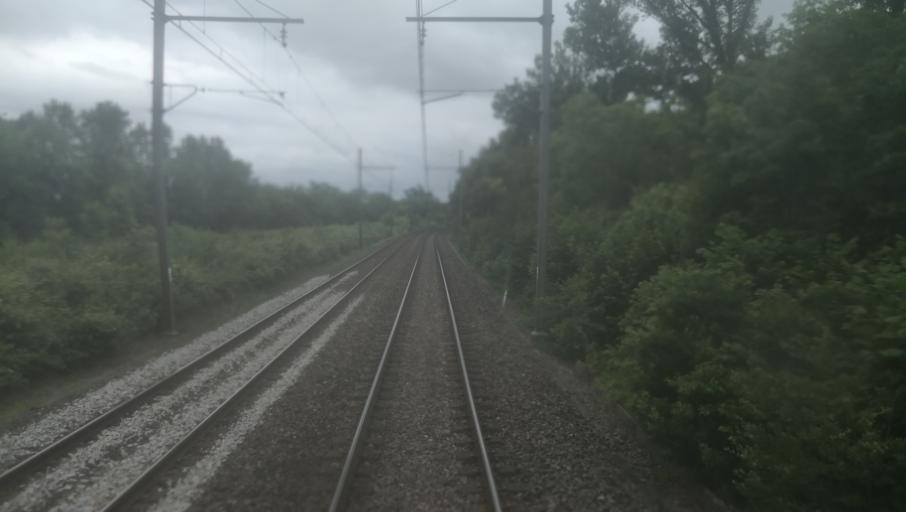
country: FR
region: Midi-Pyrenees
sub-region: Departement du Tarn-et-Garonne
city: Saint-Nicolas-de-la-Grave
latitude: 44.0930
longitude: 1.0189
